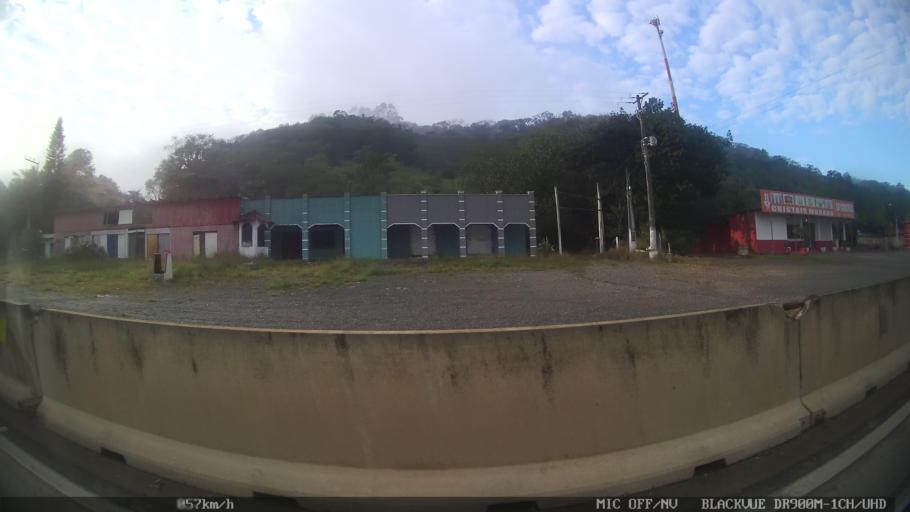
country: BR
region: Santa Catarina
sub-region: Penha
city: Penha
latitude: -26.8075
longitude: -48.6806
